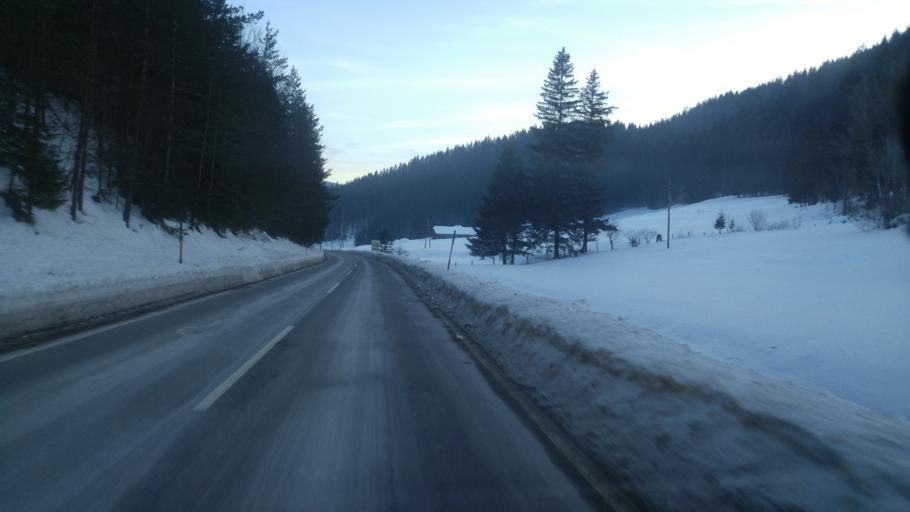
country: AT
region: Lower Austria
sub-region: Politischer Bezirk Wiener Neustadt
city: Rohr im Gebirge
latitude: 47.8758
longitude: 15.6963
